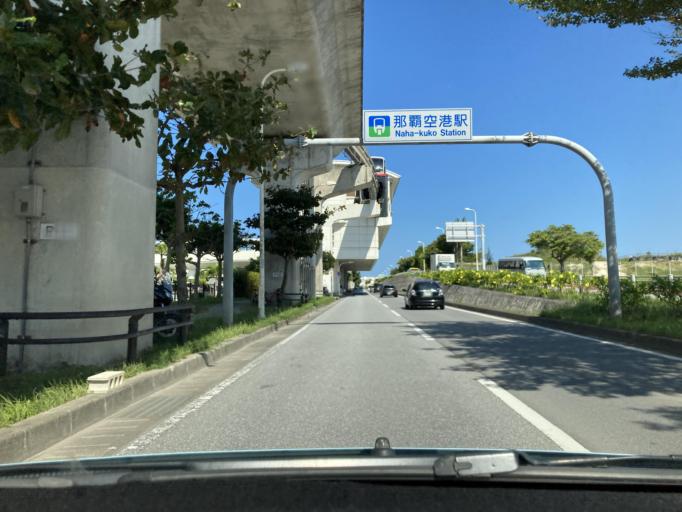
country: JP
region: Okinawa
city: Naha-shi
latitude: 26.2055
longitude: 127.6523
